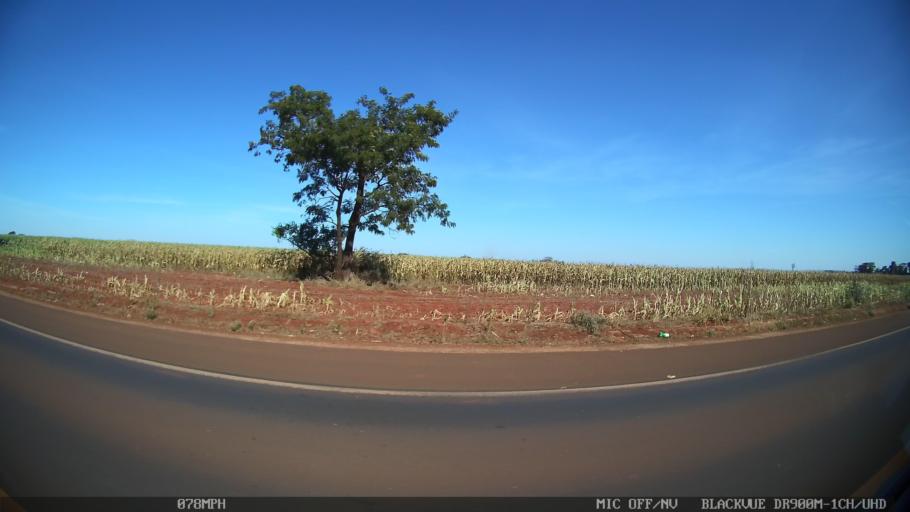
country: BR
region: Sao Paulo
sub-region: Guaira
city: Guaira
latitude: -20.4446
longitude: -48.3728
